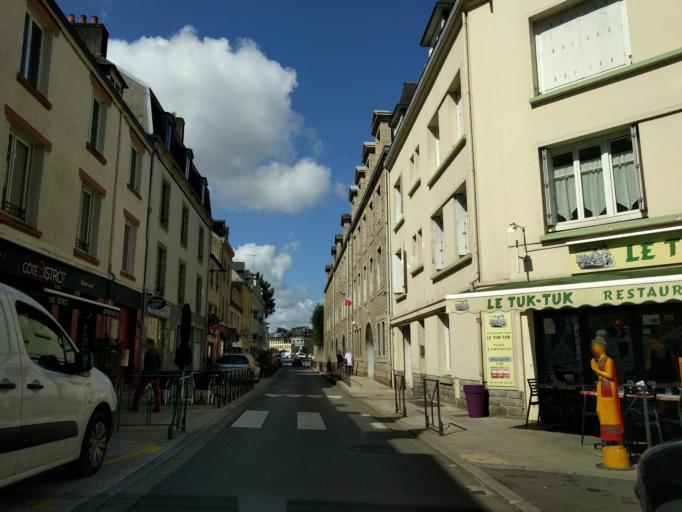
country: FR
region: Brittany
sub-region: Departement du Finistere
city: Quimper
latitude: 47.9939
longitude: -4.1025
